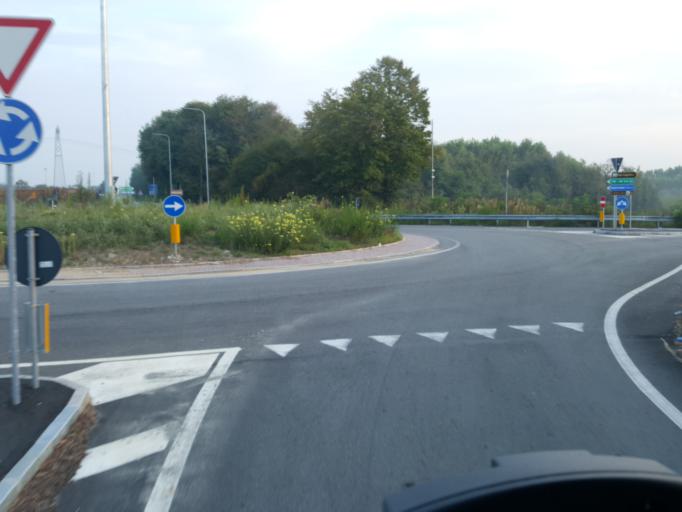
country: IT
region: Piedmont
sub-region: Provincia di Torino
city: Rondissone
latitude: 45.2358
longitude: 7.9738
